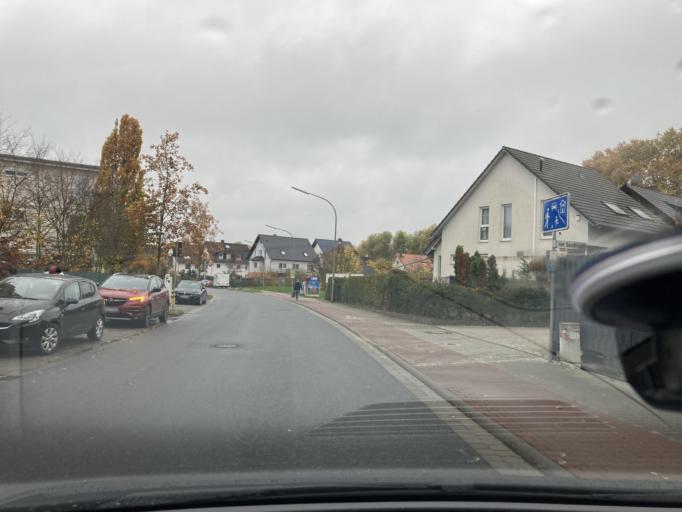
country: DE
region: Hesse
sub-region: Regierungsbezirk Darmstadt
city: Ginsheim-Gustavsburg
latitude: 49.9619
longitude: 8.3722
